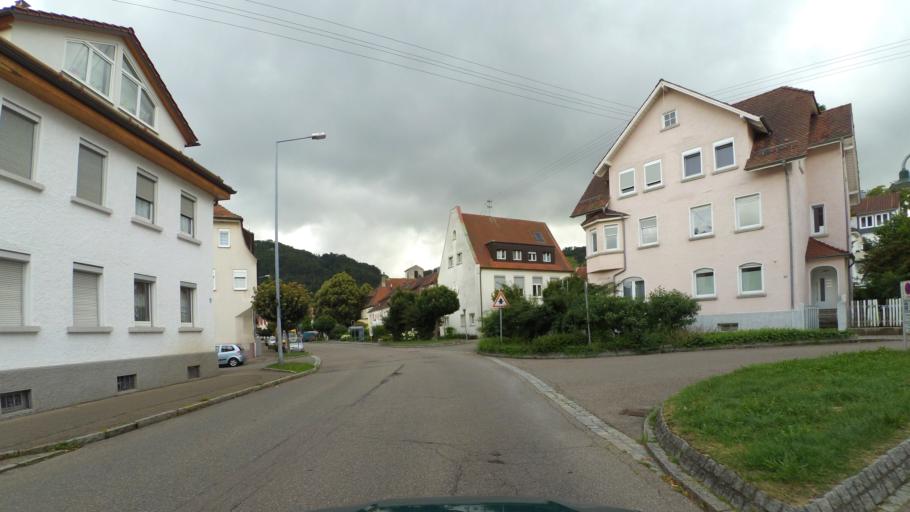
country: DE
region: Baden-Wuerttemberg
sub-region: Regierungsbezirk Stuttgart
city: Geislingen an der Steige
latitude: 48.6237
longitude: 9.8376
